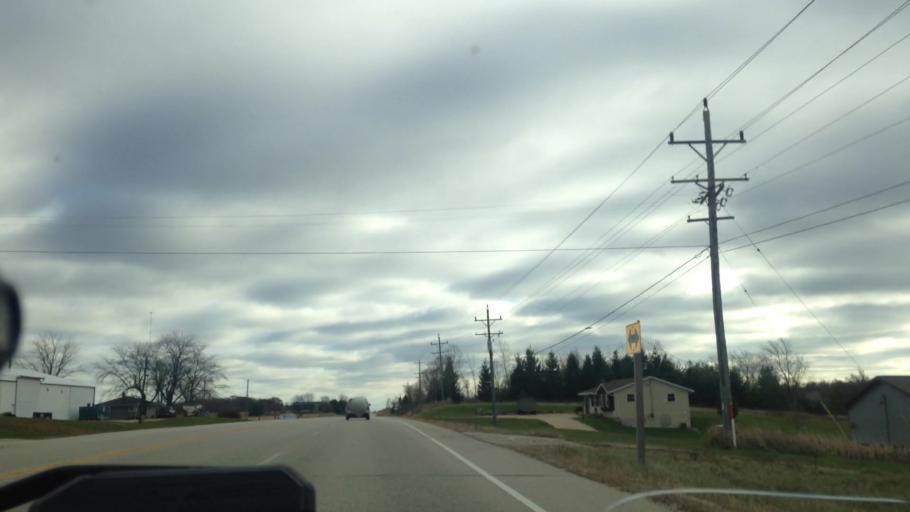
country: US
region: Wisconsin
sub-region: Washington County
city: Slinger
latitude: 43.4275
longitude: -88.2822
